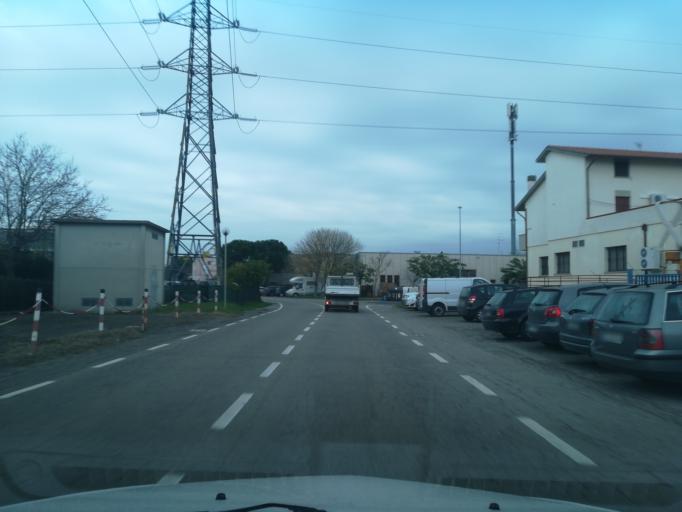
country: IT
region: Emilia-Romagna
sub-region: Provincia di Bologna
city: Imola
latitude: 44.3702
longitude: 11.7125
